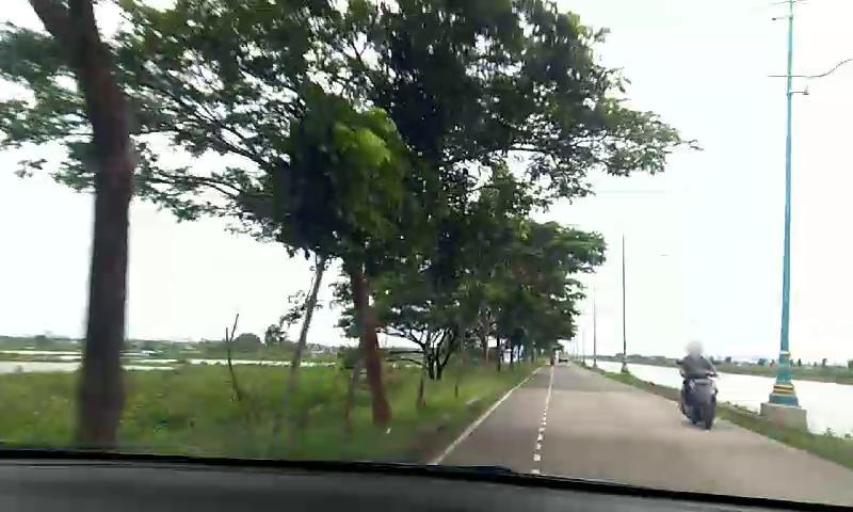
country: ID
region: West Java
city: Bekasi
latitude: -6.1242
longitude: 106.9692
